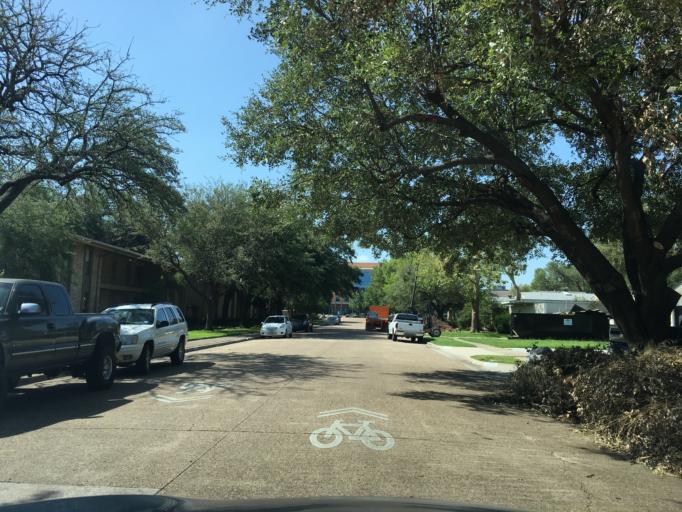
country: US
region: Texas
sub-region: Dallas County
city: Richardson
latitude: 32.9054
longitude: -96.7718
